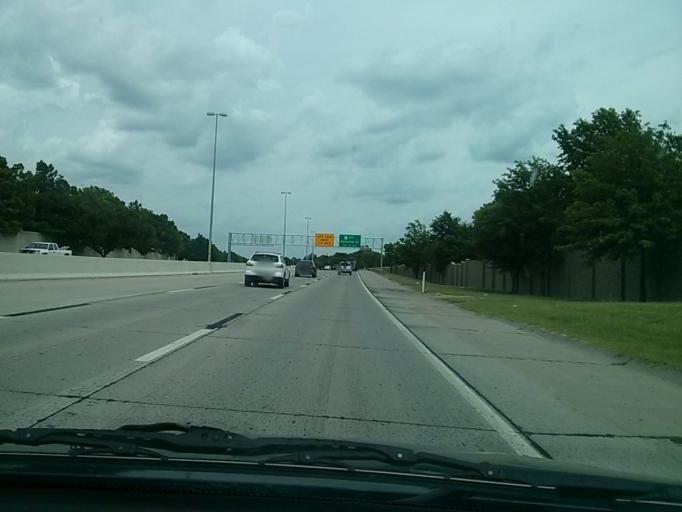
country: US
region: Oklahoma
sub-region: Tulsa County
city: Jenks
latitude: 36.0257
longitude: -95.9029
